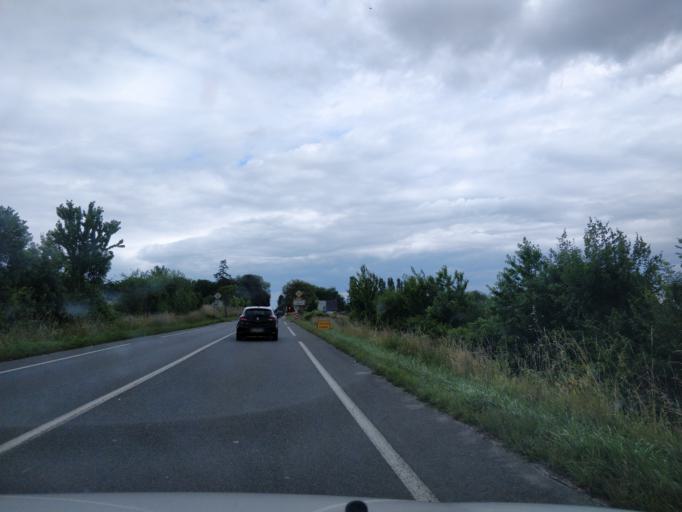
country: FR
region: Pays de la Loire
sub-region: Departement de Maine-et-Loire
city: Grez-Neuville
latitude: 47.6381
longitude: -0.6680
